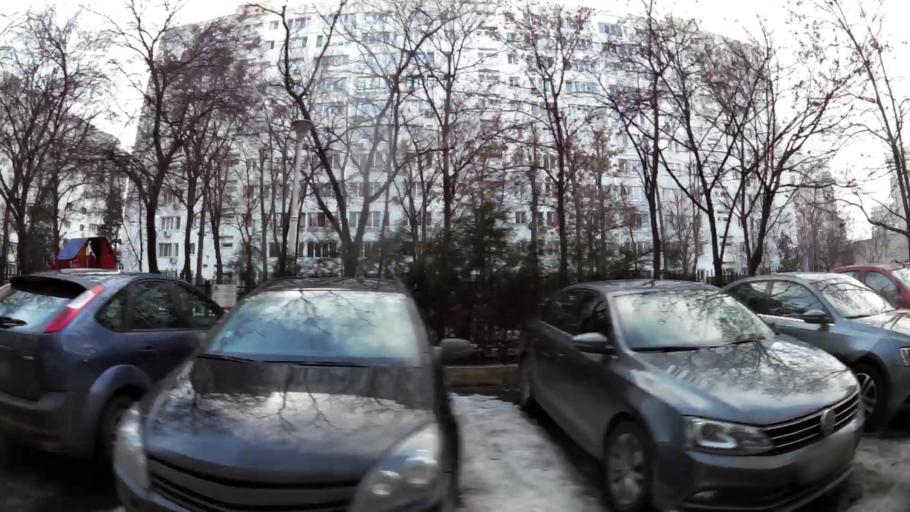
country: RO
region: Bucuresti
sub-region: Municipiul Bucuresti
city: Bucharest
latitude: 44.4213
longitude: 26.1424
